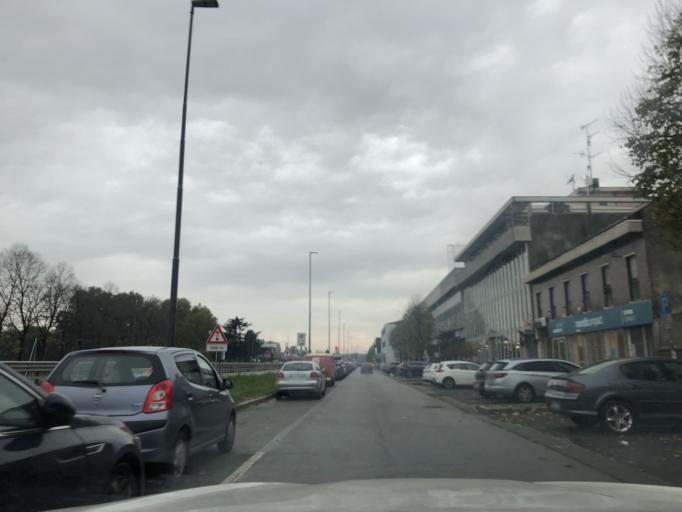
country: IT
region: Lombardy
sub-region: Citta metropolitana di Milano
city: Corsico
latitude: 45.4379
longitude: 9.1037
